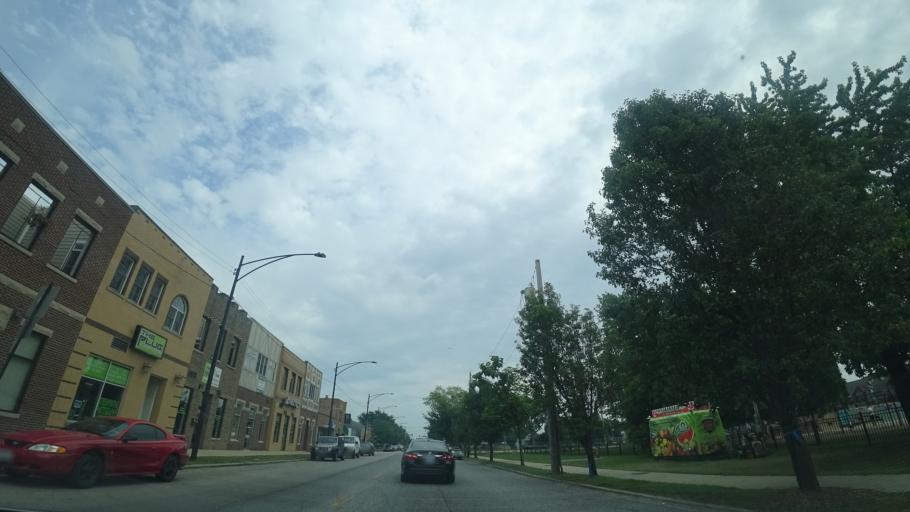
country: US
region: Illinois
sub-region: Cook County
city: Merrionette Park
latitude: 41.6913
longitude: -87.7128
